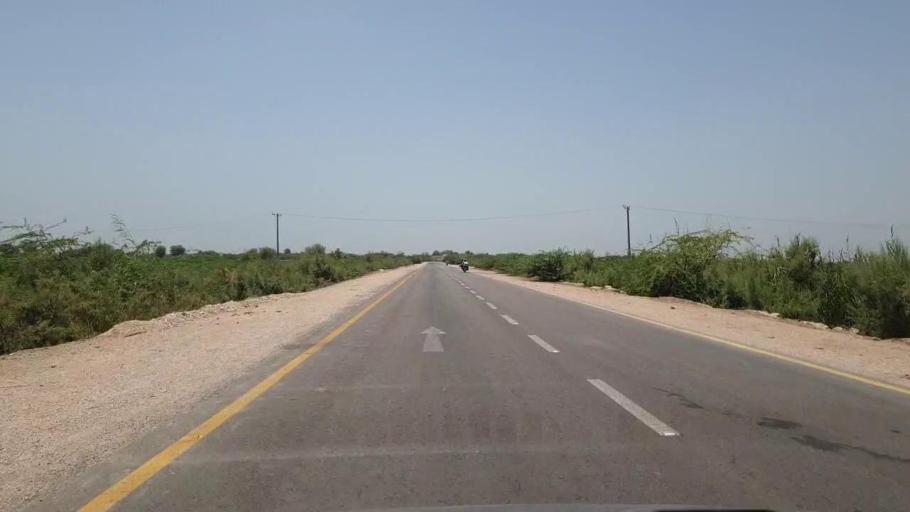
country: PK
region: Sindh
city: Sakrand
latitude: 26.1144
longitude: 68.3873
